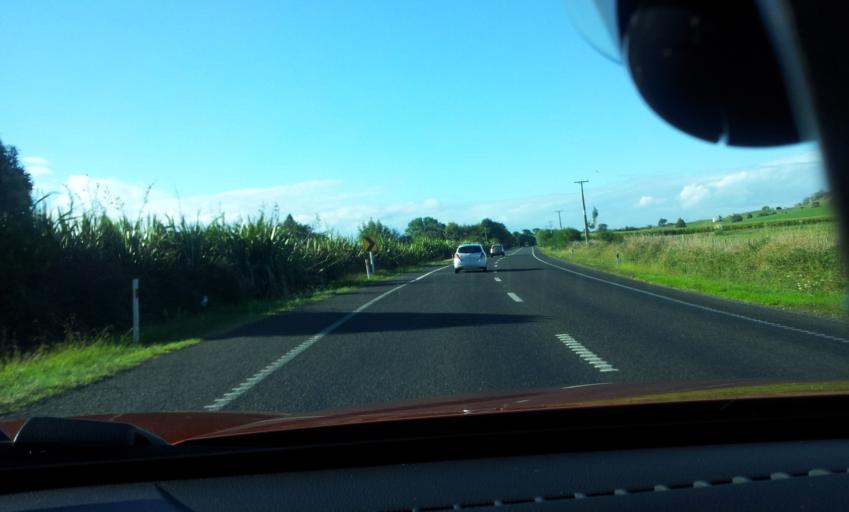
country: NZ
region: Waikato
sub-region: Hauraki District
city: Ngatea
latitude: -37.4493
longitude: 175.5077
